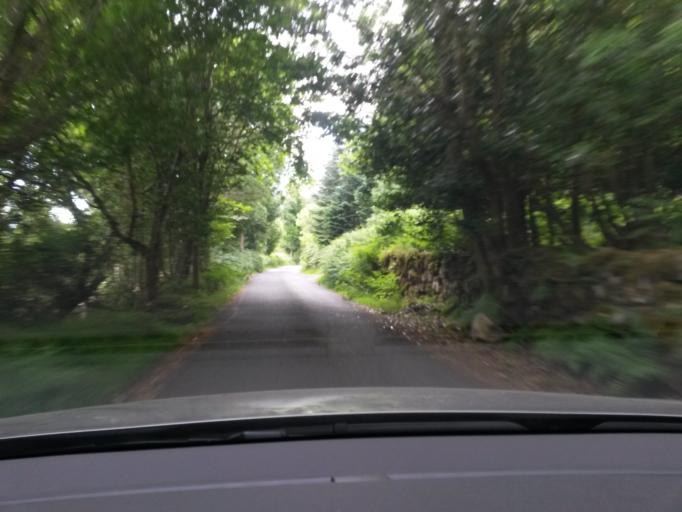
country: IE
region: Leinster
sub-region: Wicklow
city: Enniskerry
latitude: 53.1711
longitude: -6.2405
